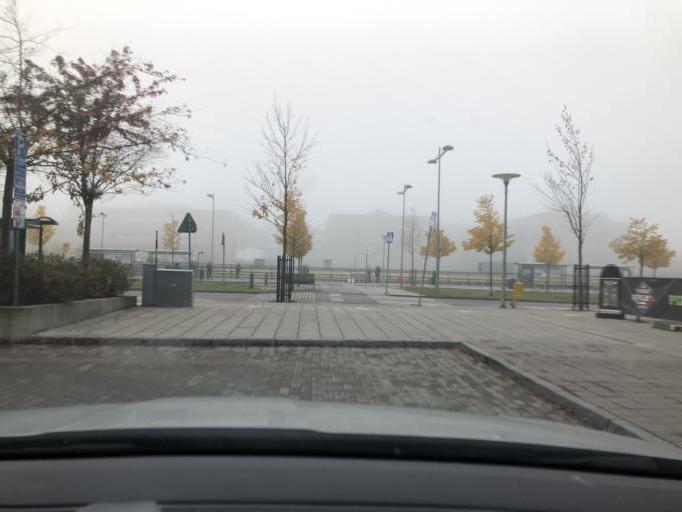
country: SE
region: Stockholm
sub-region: Botkyrka Kommun
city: Tullinge
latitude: 59.2233
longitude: 17.9376
